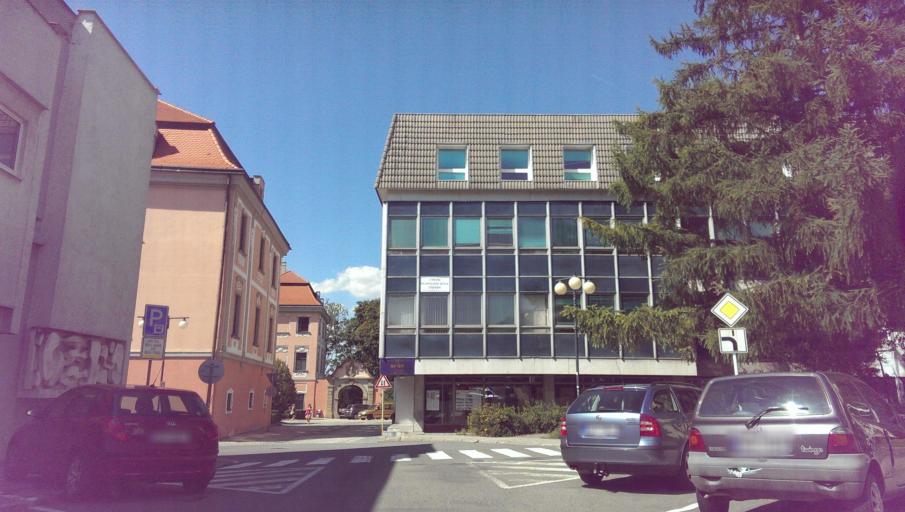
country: CZ
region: Zlin
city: Valasske Mezirici
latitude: 49.4711
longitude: 17.9703
